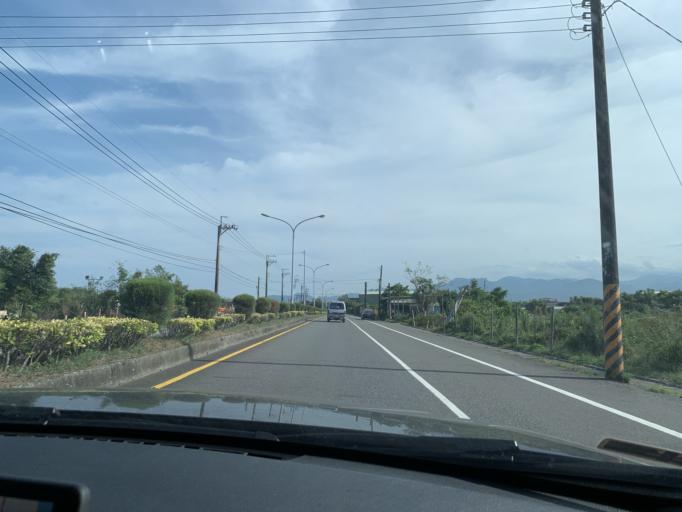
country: TW
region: Taiwan
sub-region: Yilan
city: Yilan
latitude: 24.7427
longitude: 121.8166
